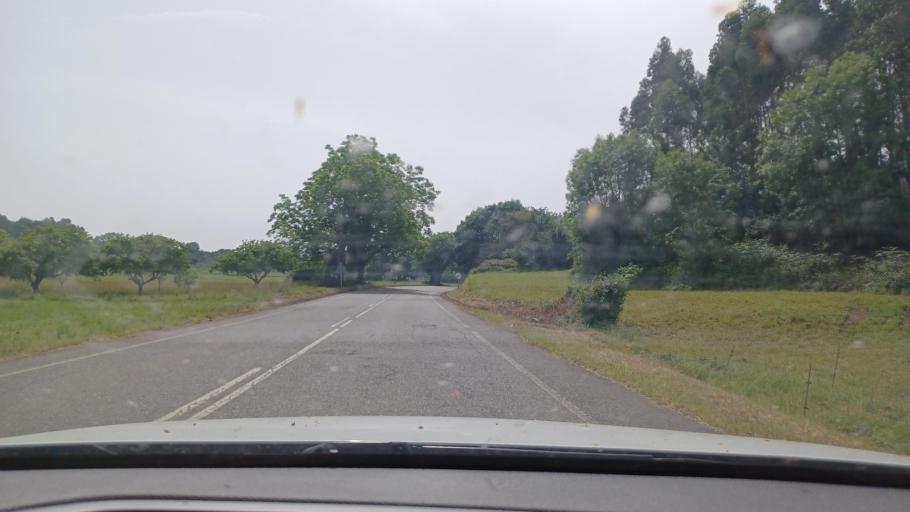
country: ES
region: Asturias
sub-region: Province of Asturias
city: Ribadesella
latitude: 43.4521
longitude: -5.0277
